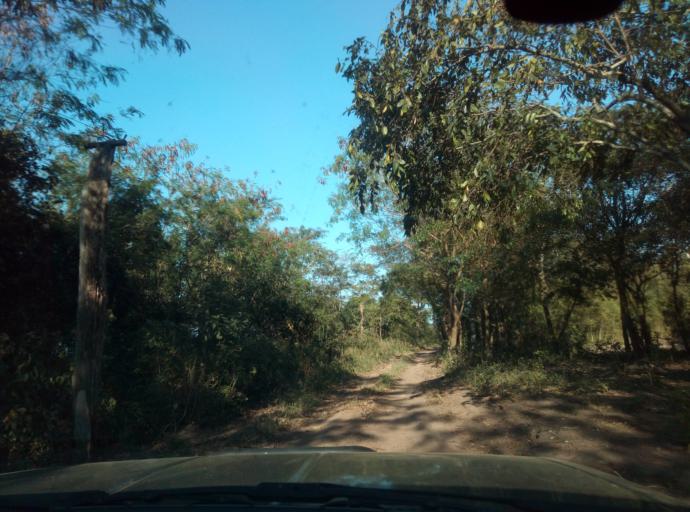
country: PY
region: Caaguazu
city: San Joaquin
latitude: -25.1681
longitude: -56.1124
